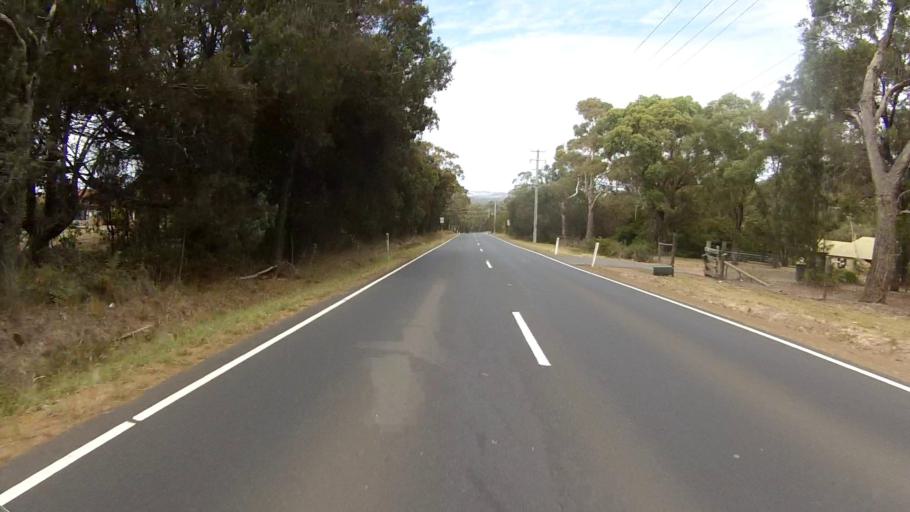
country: AU
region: Tasmania
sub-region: Clarence
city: Acton Park
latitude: -42.8818
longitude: 147.4822
